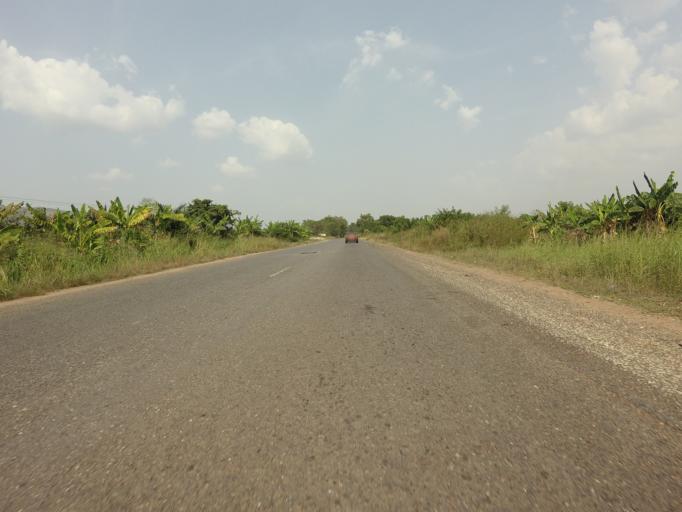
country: GH
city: Akropong
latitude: 5.9449
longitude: -0.0206
